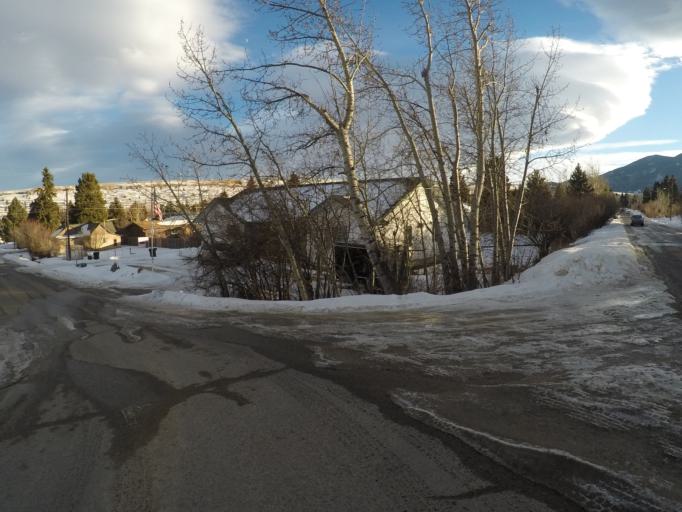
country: US
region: Montana
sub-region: Carbon County
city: Red Lodge
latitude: 45.1799
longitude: -109.2547
